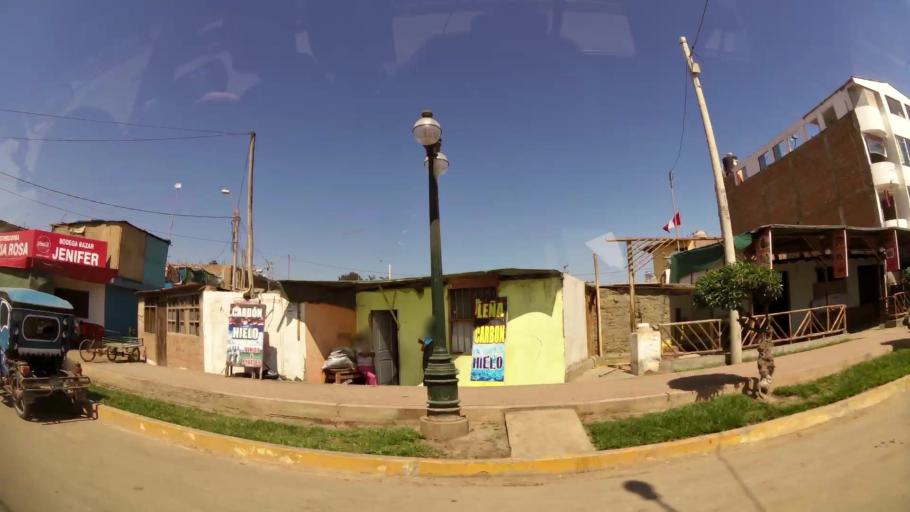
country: PE
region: Lima
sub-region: Provincia de Canete
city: San Vicente de Canete
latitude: -13.0240
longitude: -76.4762
